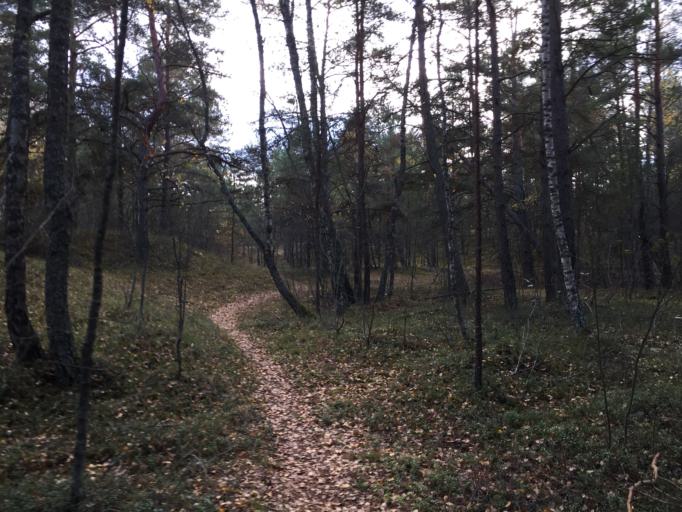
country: LV
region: Carnikava
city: Carnikava
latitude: 57.1503
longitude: 24.2600
